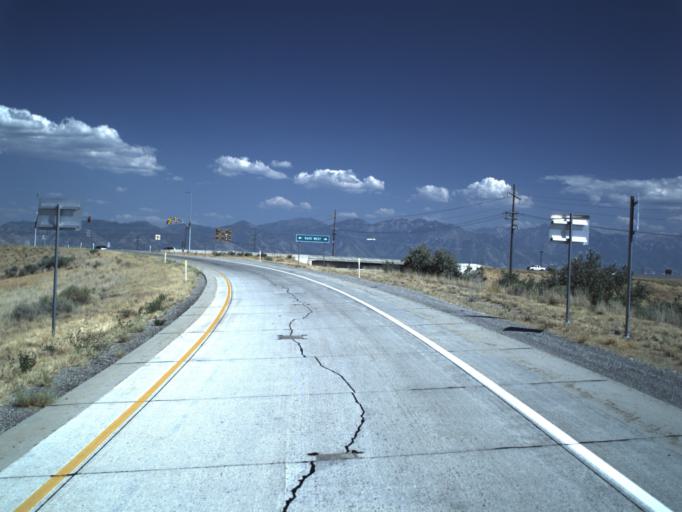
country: US
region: Utah
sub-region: Salt Lake County
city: West Valley City
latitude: 40.7694
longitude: -112.0274
